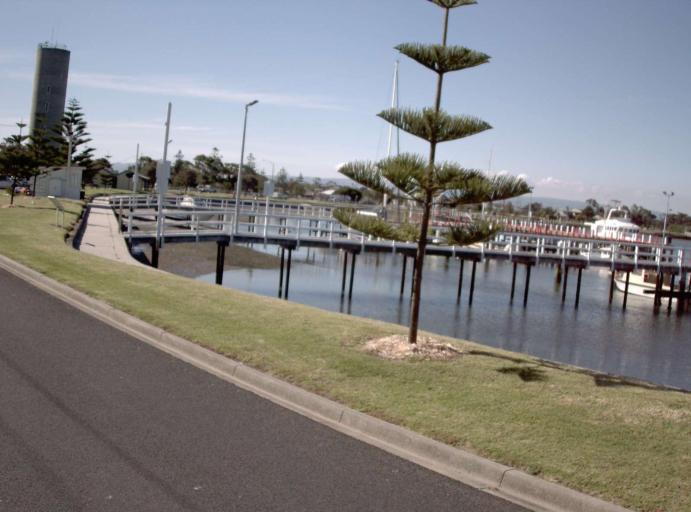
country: AU
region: Victoria
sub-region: Latrobe
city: Traralgon
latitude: -38.6740
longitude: 146.6953
